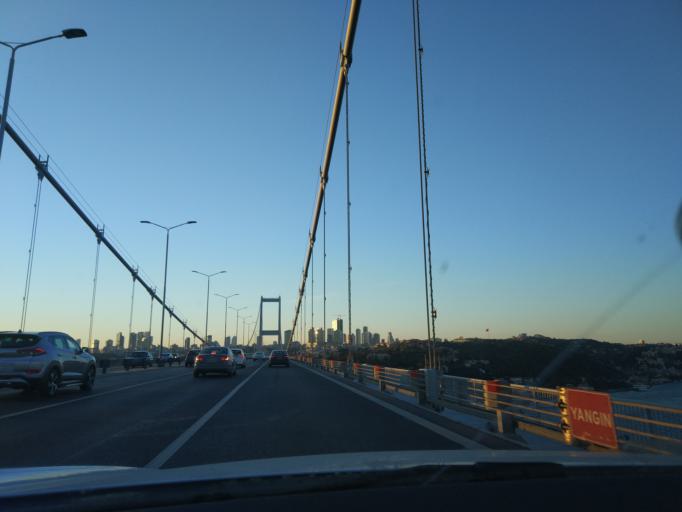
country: TR
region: Istanbul
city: UEskuedar
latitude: 41.0437
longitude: 29.0364
